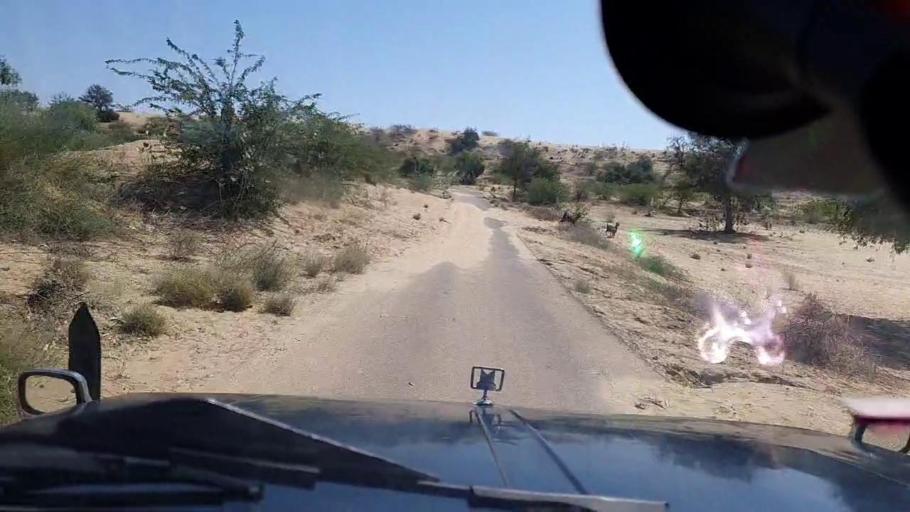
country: PK
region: Sindh
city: Diplo
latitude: 24.5623
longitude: 69.6736
